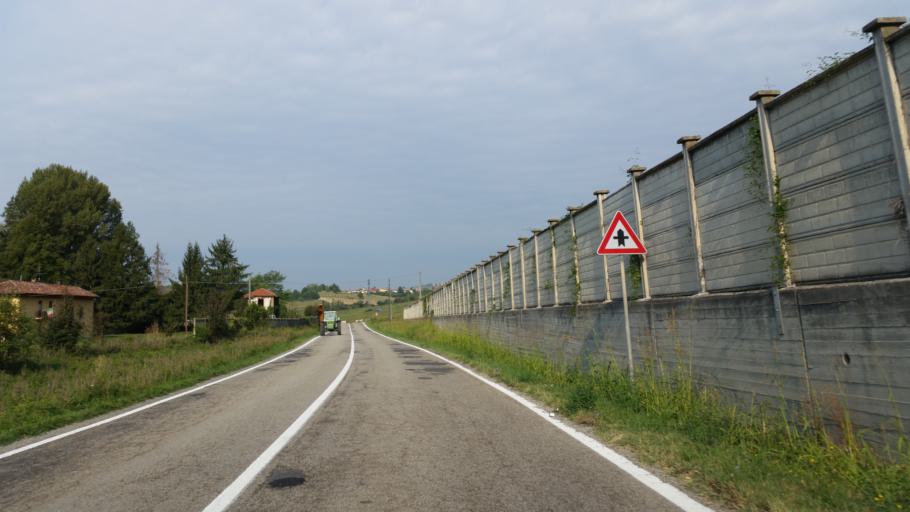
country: IT
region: Piedmont
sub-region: Provincia di Asti
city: Montiglio
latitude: 45.0756
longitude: 8.0973
